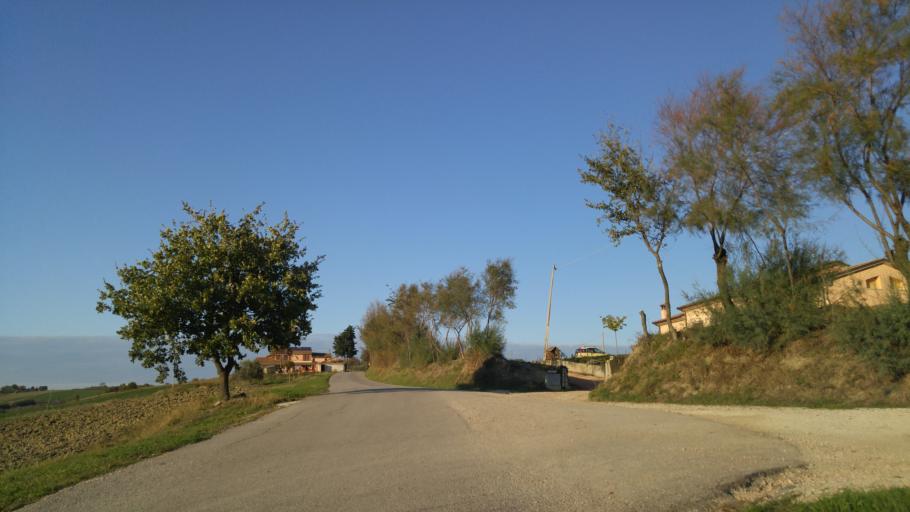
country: IT
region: The Marches
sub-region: Provincia di Pesaro e Urbino
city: Cartoceto
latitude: 43.7888
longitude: 12.8990
